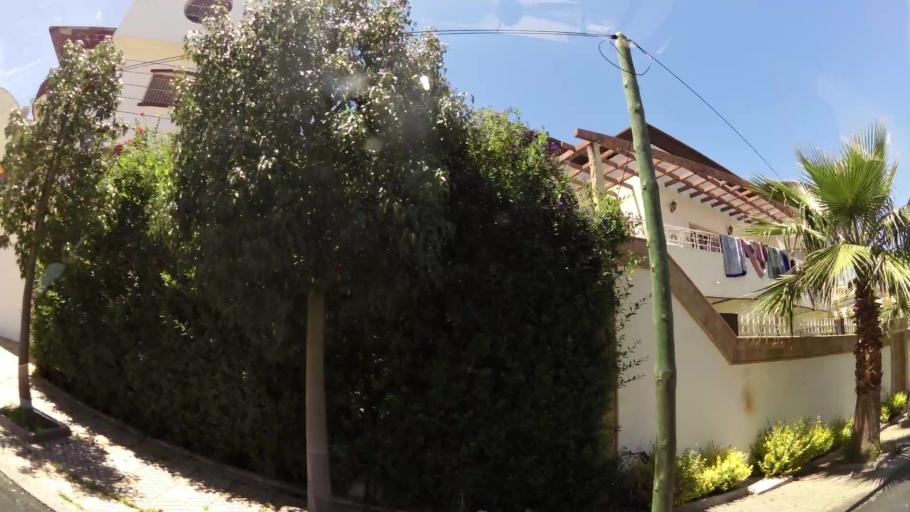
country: MA
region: Meknes-Tafilalet
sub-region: Meknes
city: Meknes
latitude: 33.9037
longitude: -5.5492
